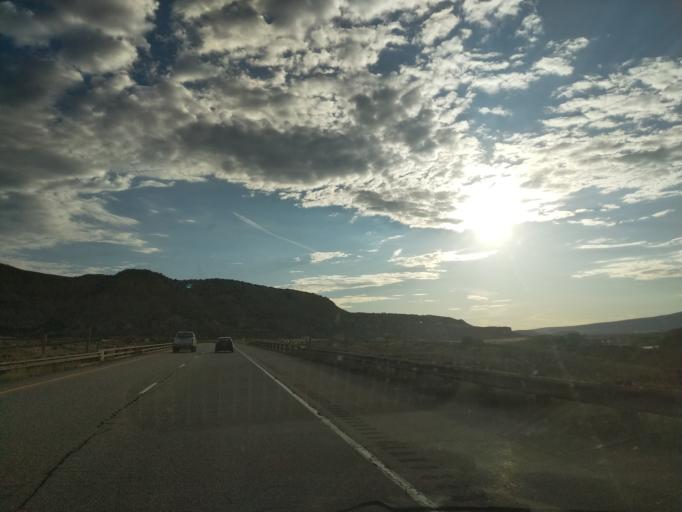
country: US
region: Colorado
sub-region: Garfield County
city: Battlement Mesa
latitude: 39.4970
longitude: -107.9423
